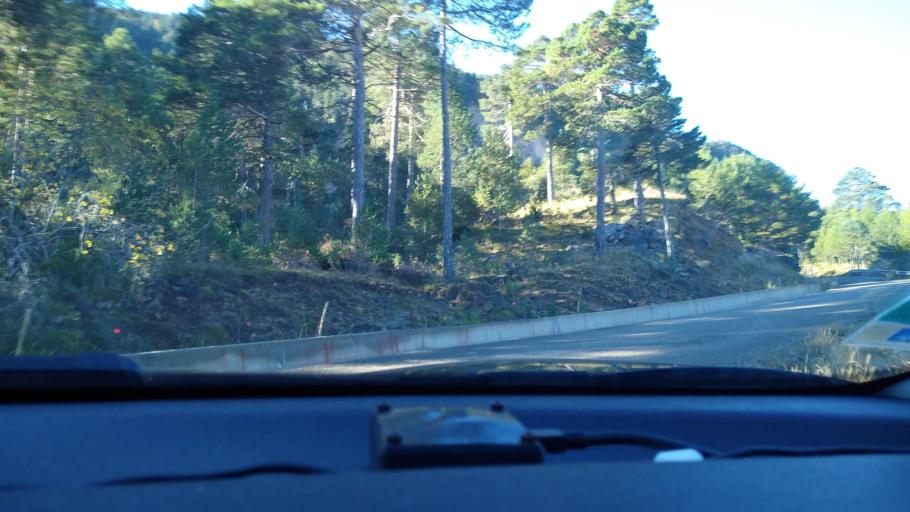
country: ES
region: Catalonia
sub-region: Provincia de Barcelona
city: Saldes
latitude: 42.2061
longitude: 1.7287
